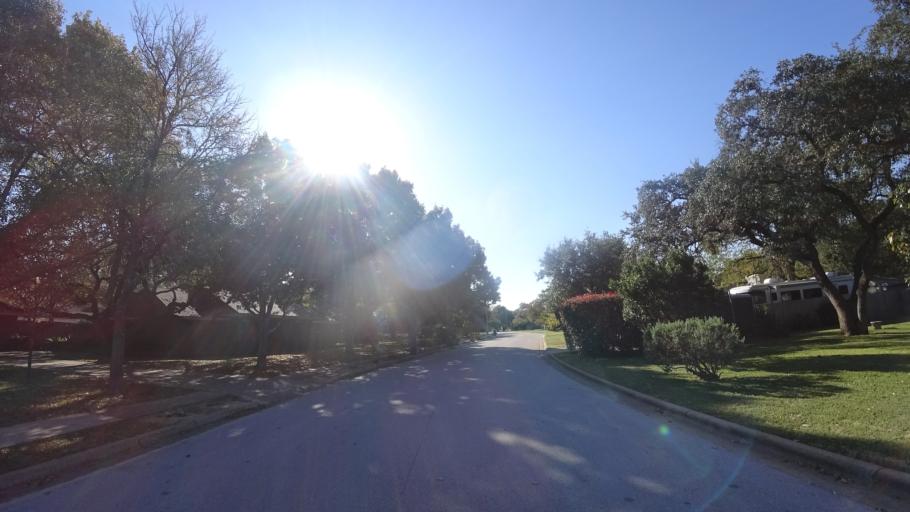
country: US
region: Texas
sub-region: Travis County
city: Shady Hollow
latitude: 30.2224
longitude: -97.8487
